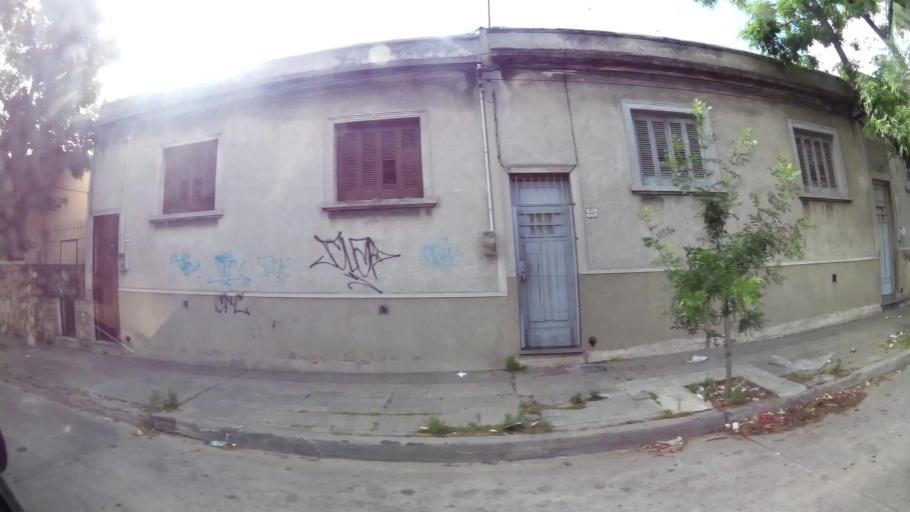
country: UY
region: Montevideo
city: Montevideo
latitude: -34.8815
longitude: -56.1585
